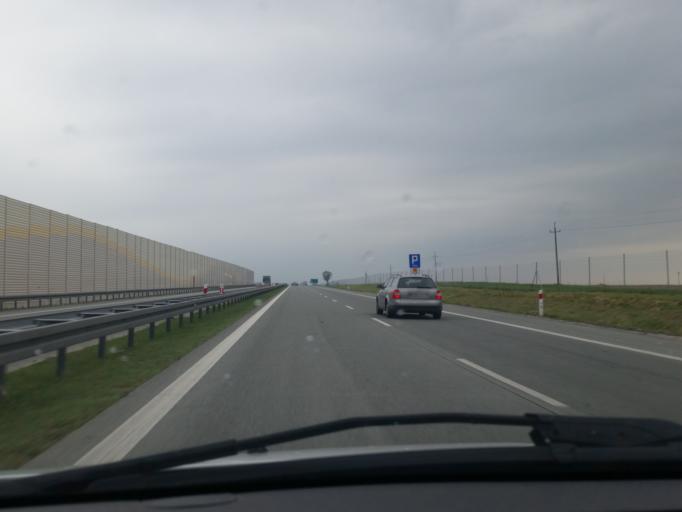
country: PL
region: Lodz Voivodeship
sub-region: Powiat skierniewicki
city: Kowiesy
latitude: 51.8524
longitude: 20.3709
